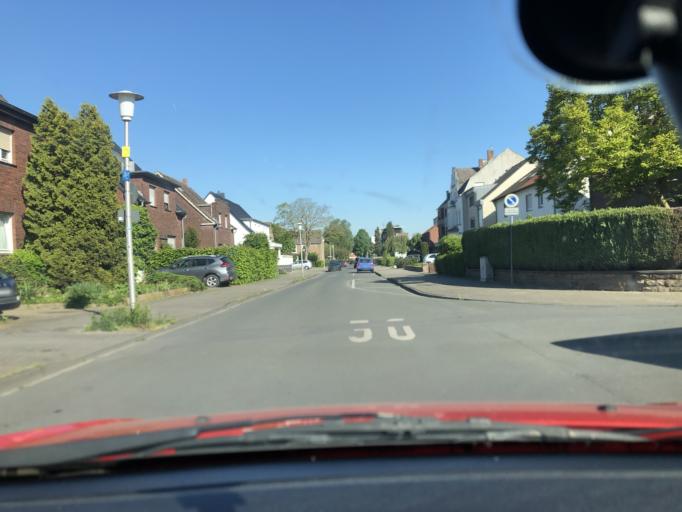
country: DE
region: North Rhine-Westphalia
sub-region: Regierungsbezirk Dusseldorf
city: Kamp-Lintfort
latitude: 51.4975
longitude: 6.5322
